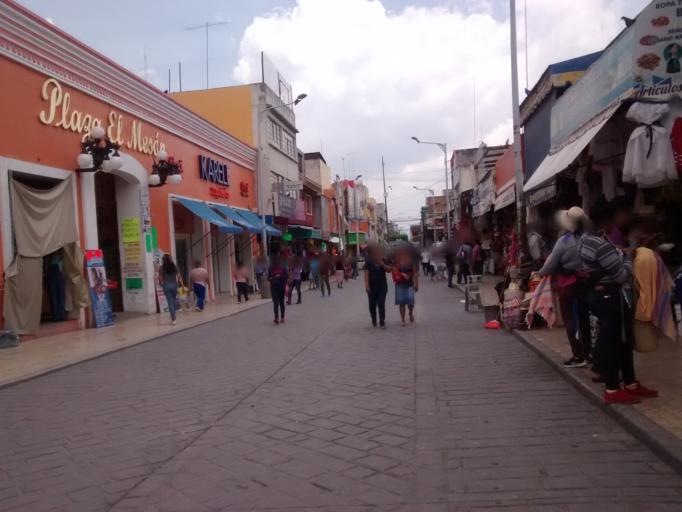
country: MX
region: Puebla
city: Tehuacan
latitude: 18.4615
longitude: -97.3907
